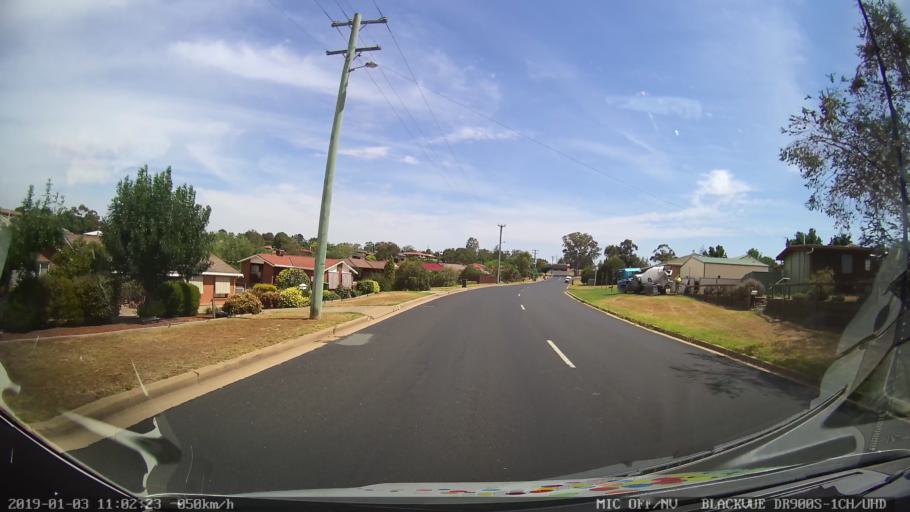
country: AU
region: New South Wales
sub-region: Young
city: Young
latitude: -34.2984
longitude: 148.2986
